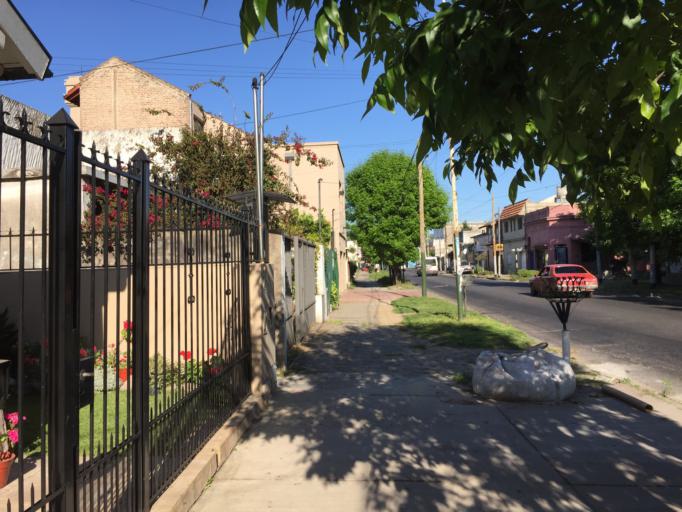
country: AR
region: Buenos Aires
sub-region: Partido de Lomas de Zamora
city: Lomas de Zamora
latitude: -34.7369
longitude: -58.3882
